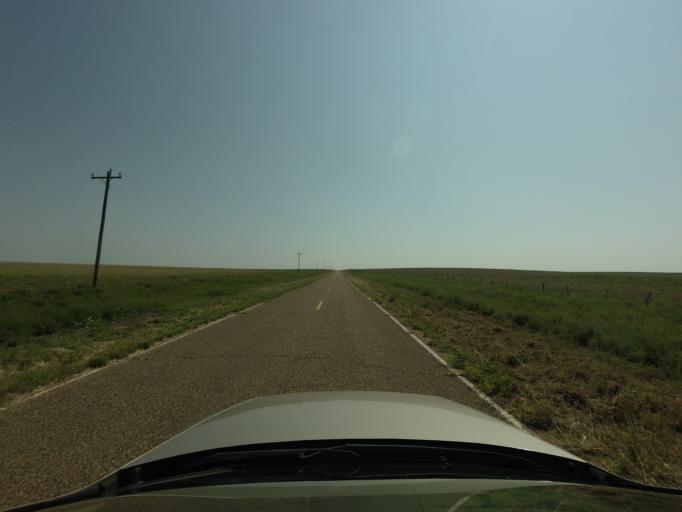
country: US
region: New Mexico
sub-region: Curry County
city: Cannon Air Force Base
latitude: 34.6335
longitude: -103.5867
